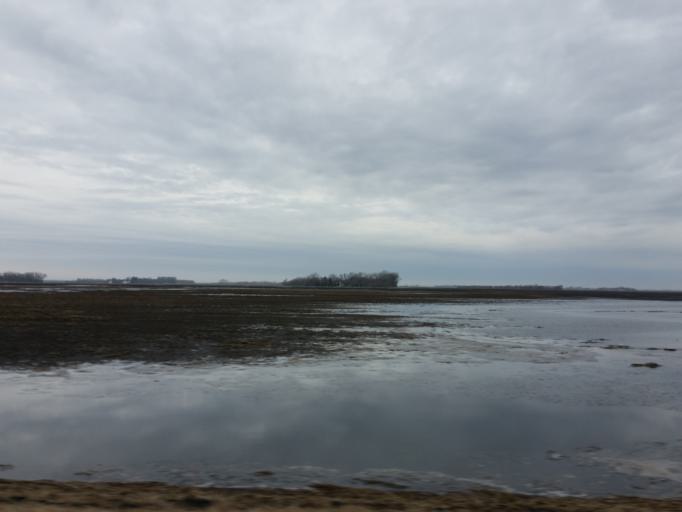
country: US
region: North Dakota
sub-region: Walsh County
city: Grafton
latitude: 48.3900
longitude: -97.4703
